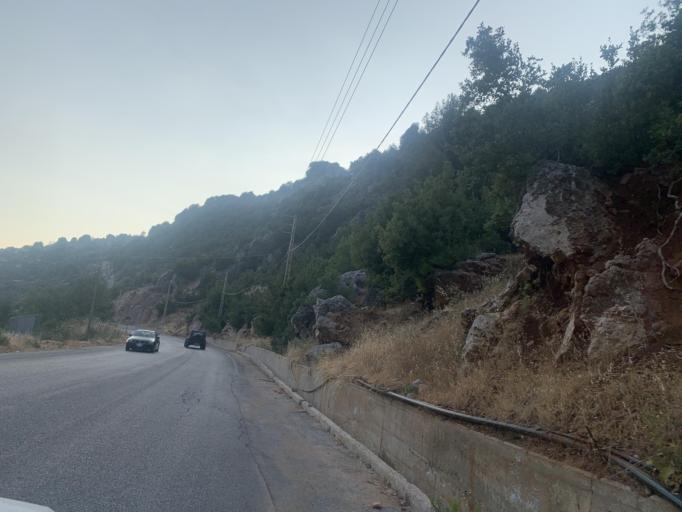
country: LB
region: Liban-Nord
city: Amioun
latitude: 34.1333
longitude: 35.8181
